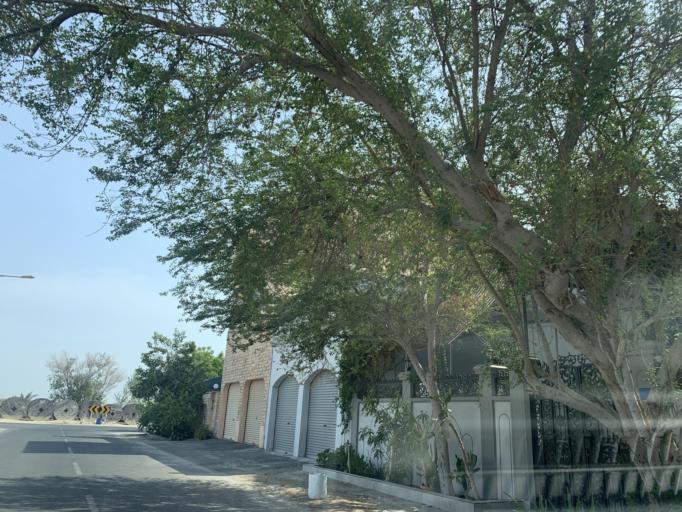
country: BH
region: Muharraq
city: Al Hadd
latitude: 26.2638
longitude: 50.6571
